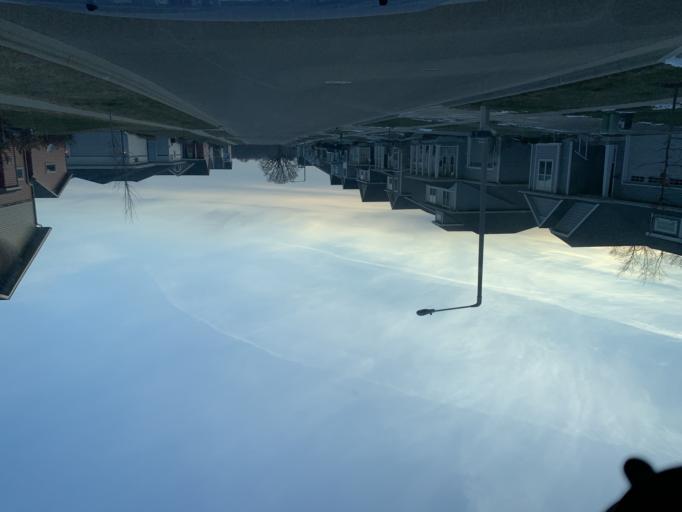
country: US
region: Wisconsin
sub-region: Dane County
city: Middleton
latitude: 43.0573
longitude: -89.5641
